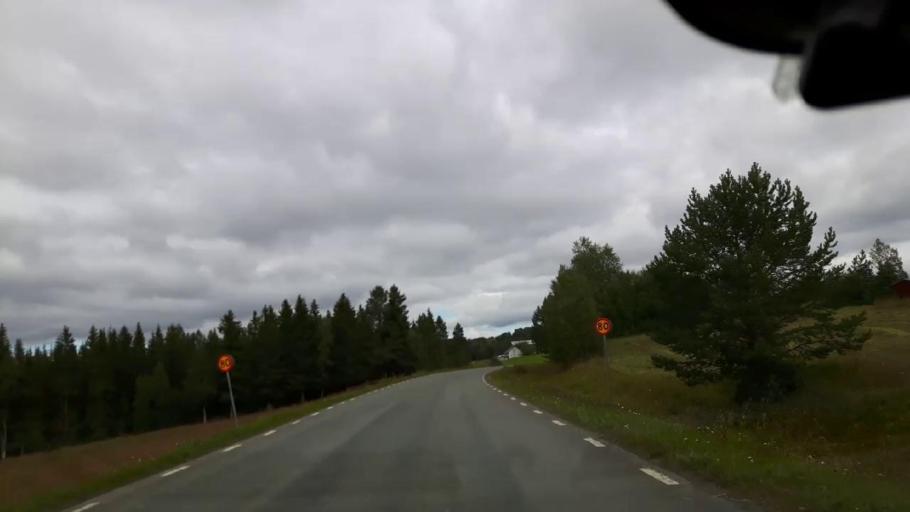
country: SE
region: Jaemtland
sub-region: Krokoms Kommun
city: Valla
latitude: 63.5005
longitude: 13.8956
